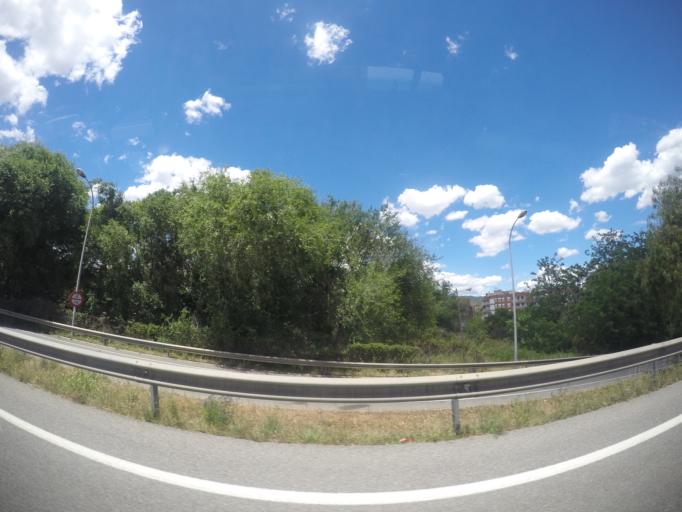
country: ES
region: Catalonia
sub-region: Provincia de Barcelona
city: Badalona
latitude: 41.4564
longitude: 2.2476
